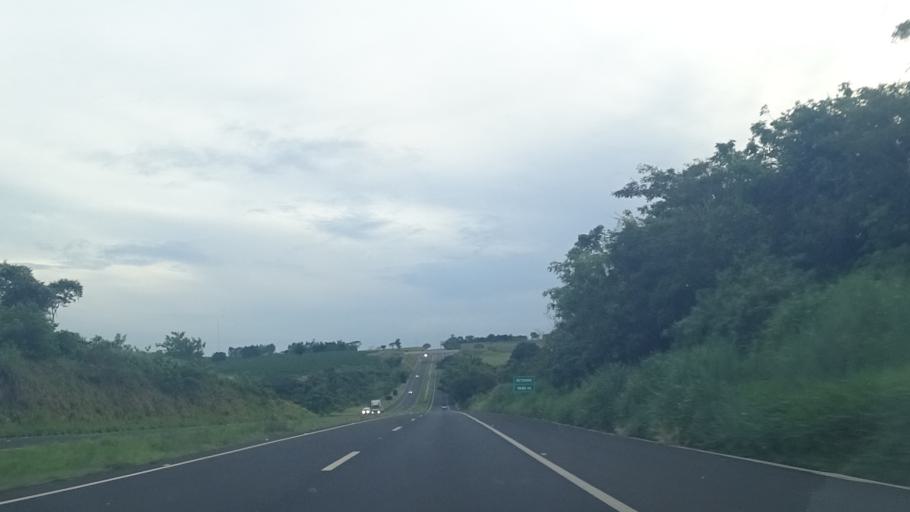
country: BR
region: Sao Paulo
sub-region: Martinopolis
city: Martinopolis
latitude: -22.1427
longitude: -51.2343
